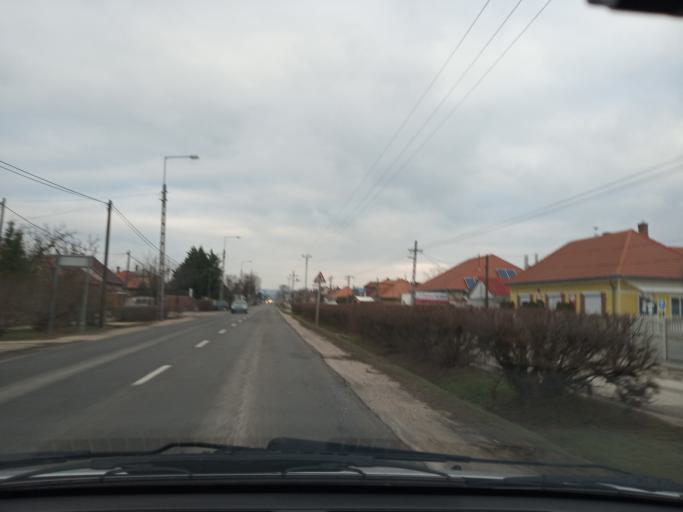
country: HU
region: Komarom-Esztergom
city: Dorog
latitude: 47.7395
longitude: 18.7268
